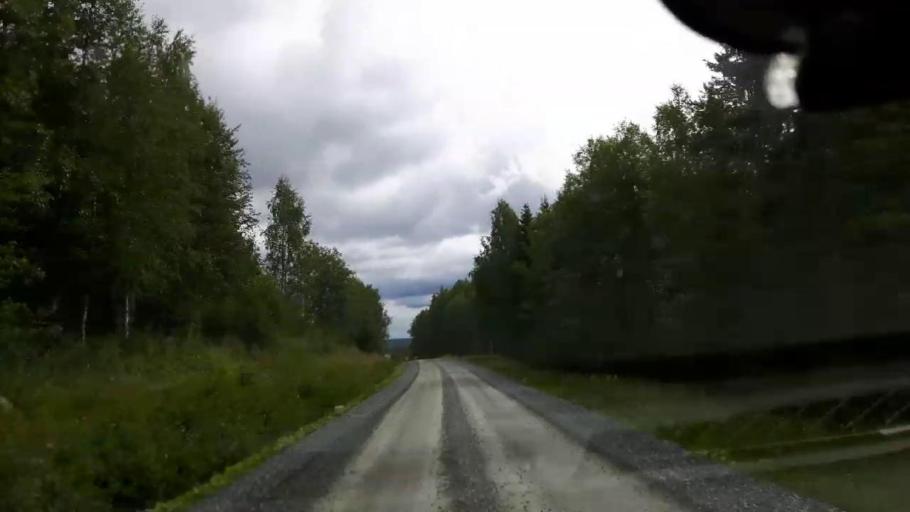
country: SE
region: Jaemtland
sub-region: Krokoms Kommun
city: Valla
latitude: 63.5877
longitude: 14.1500
